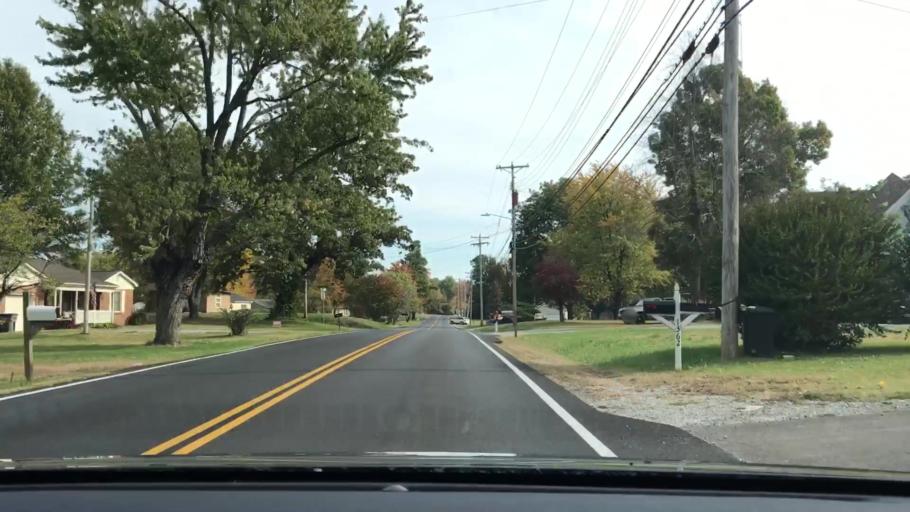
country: US
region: Kentucky
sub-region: Graves County
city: Mayfield
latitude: 36.7405
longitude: -88.6638
